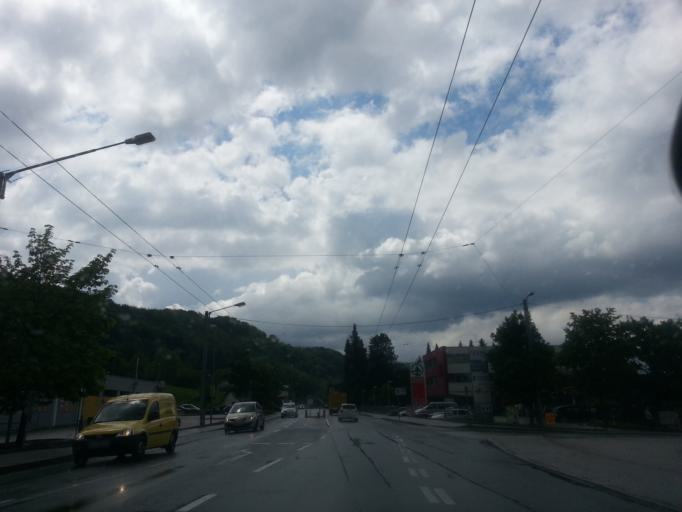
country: AT
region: Salzburg
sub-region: Politischer Bezirk Salzburg-Umgebung
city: Hallwang
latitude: 47.8257
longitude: 13.0798
